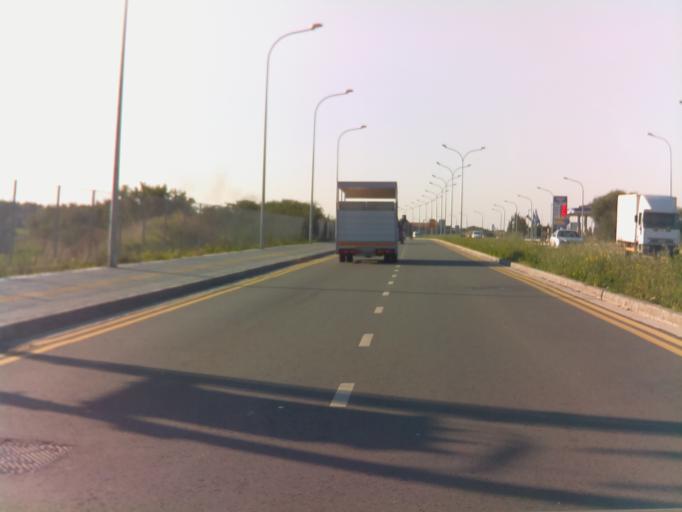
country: CY
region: Limassol
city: Pano Polemidia
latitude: 34.6779
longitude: 32.9897
